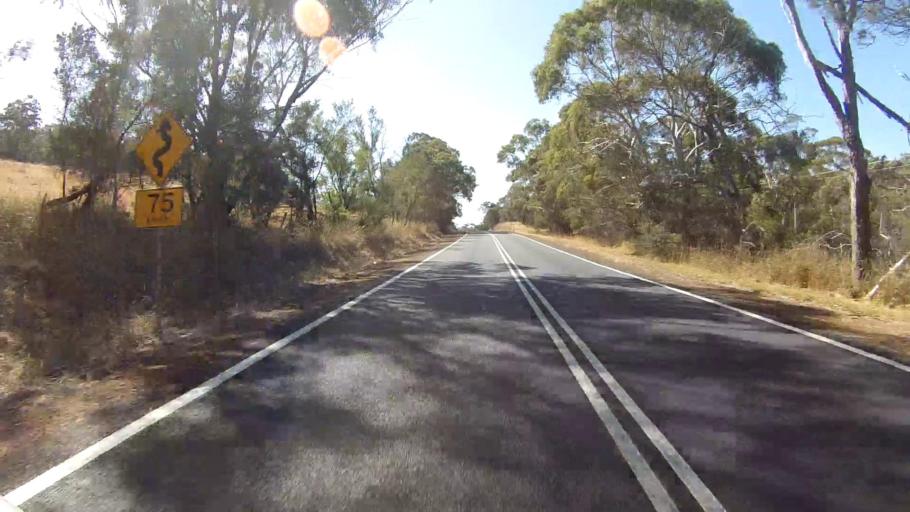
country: AU
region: Tasmania
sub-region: Sorell
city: Sorell
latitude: -42.3966
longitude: 147.9330
